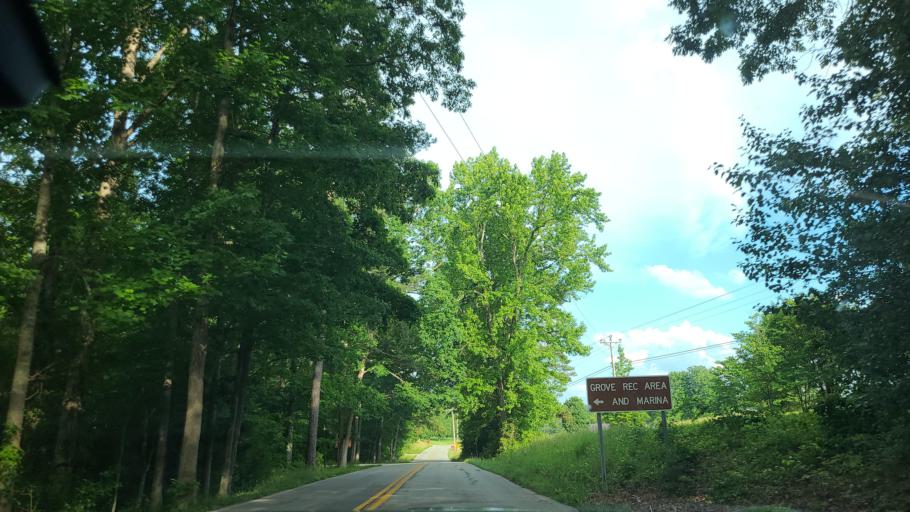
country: US
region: Kentucky
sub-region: Whitley County
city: Corbin
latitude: 36.9054
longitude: -84.2398
